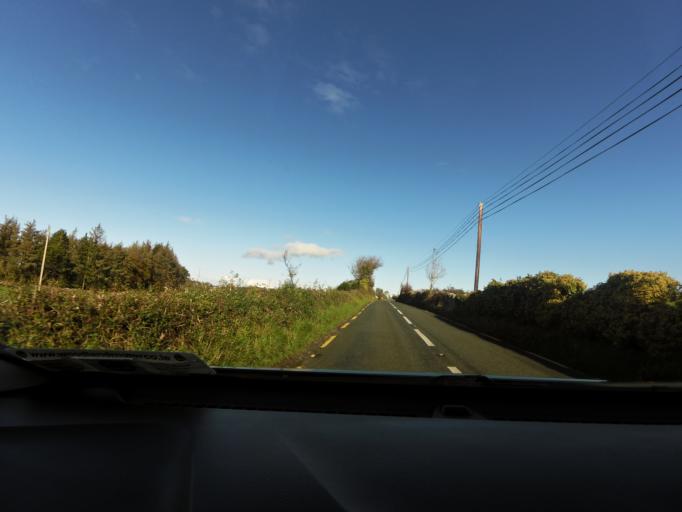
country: IE
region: Connaught
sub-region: Maigh Eo
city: Ballinrobe
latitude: 53.5335
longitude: -9.0933
